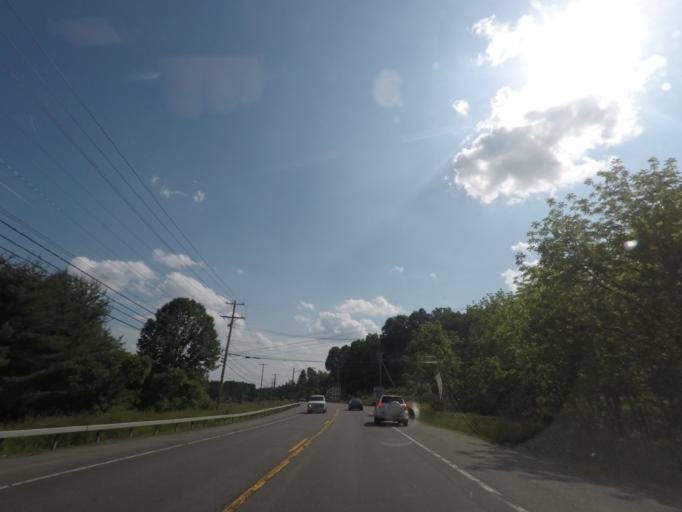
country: US
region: New York
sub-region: Ulster County
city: Marlboro
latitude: 41.5831
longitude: -73.9861
